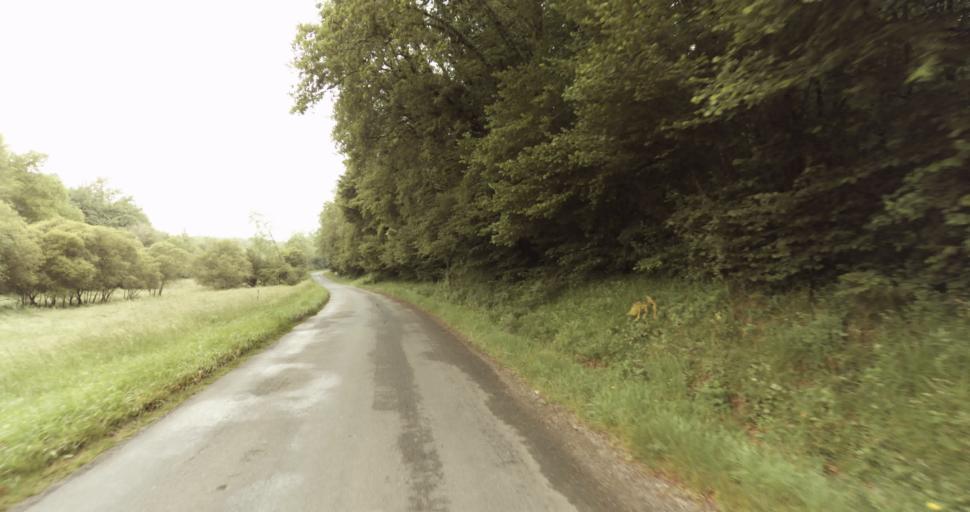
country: FR
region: Aquitaine
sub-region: Departement de la Dordogne
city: Lalinde
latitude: 44.8848
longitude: 0.7749
